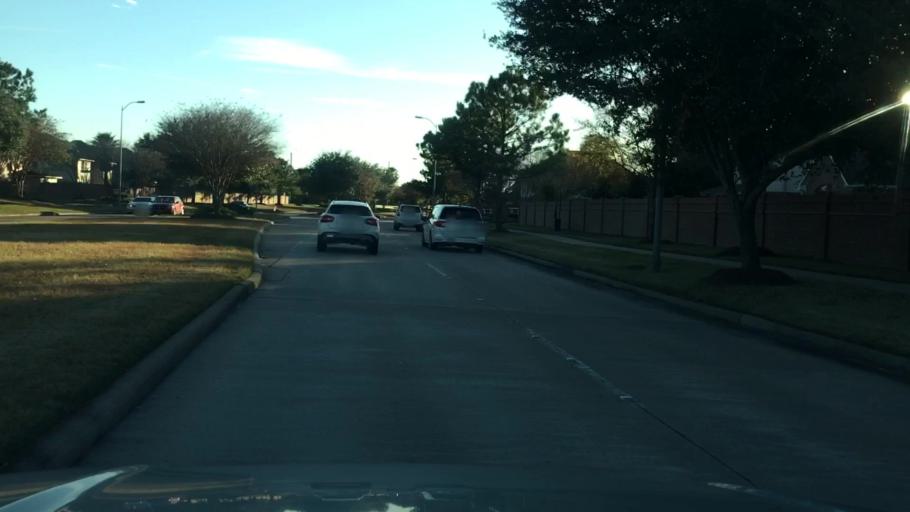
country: US
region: Texas
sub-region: Fort Bend County
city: Cinco Ranch
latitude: 29.7520
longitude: -95.7847
